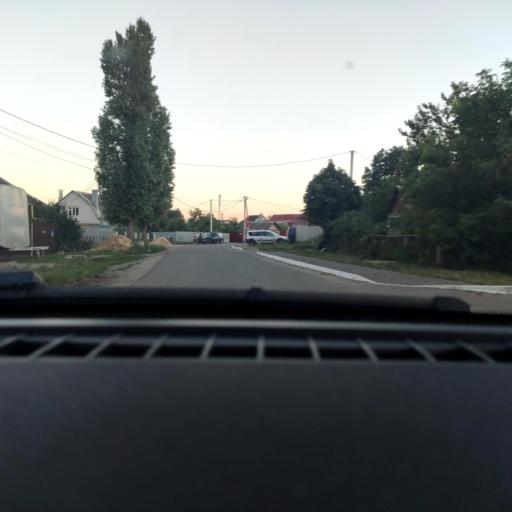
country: RU
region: Voronezj
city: Novaya Usman'
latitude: 51.6573
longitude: 39.3382
